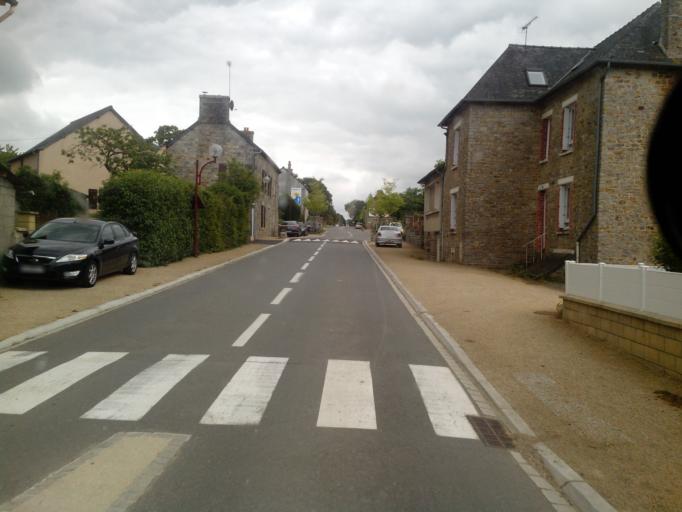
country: FR
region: Brittany
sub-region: Departement d'Ille-et-Vilaine
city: Chasne-sur-Illet
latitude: 48.2428
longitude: -1.5596
